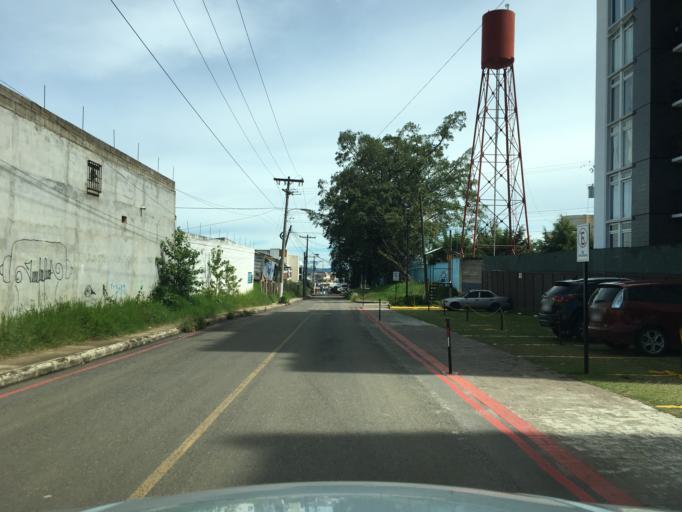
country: GT
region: Guatemala
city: Mixco
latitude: 14.6573
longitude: -90.5634
